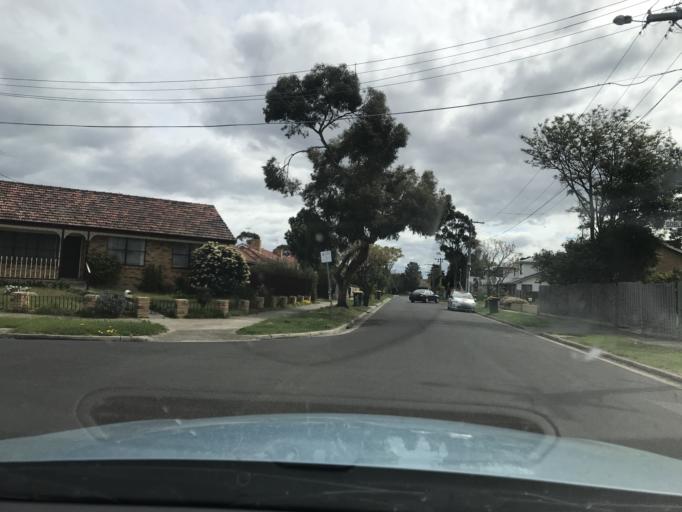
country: AU
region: Victoria
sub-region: Hobsons Bay
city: Laverton
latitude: -37.8618
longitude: 144.7689
